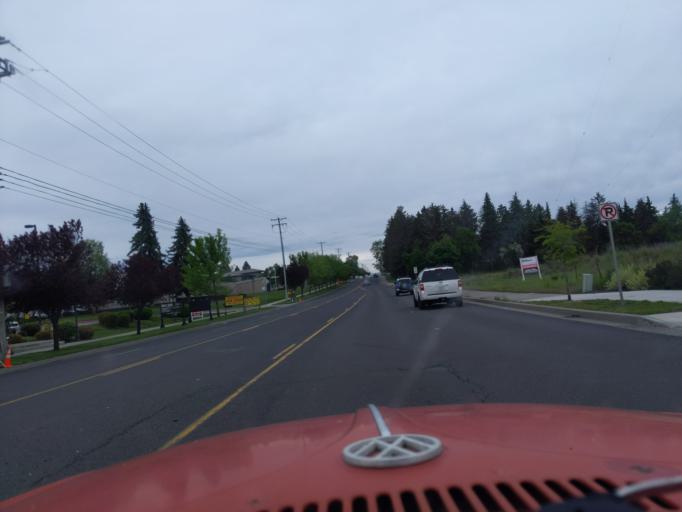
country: US
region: Washington
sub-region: Spokane County
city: Spokane
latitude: 47.6141
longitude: -117.3685
